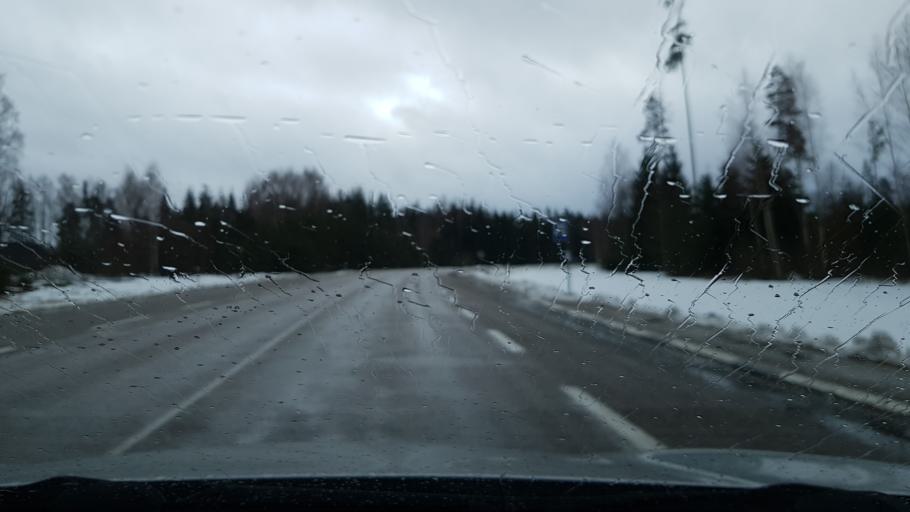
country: LV
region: Apes Novads
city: Ape
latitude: 57.6243
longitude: 26.6380
